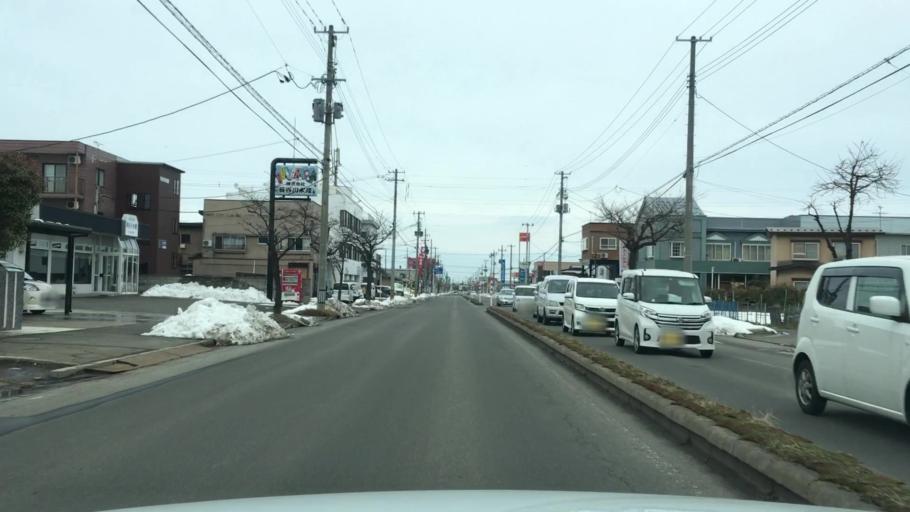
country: JP
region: Aomori
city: Hirosaki
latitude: 40.5970
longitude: 140.4923
